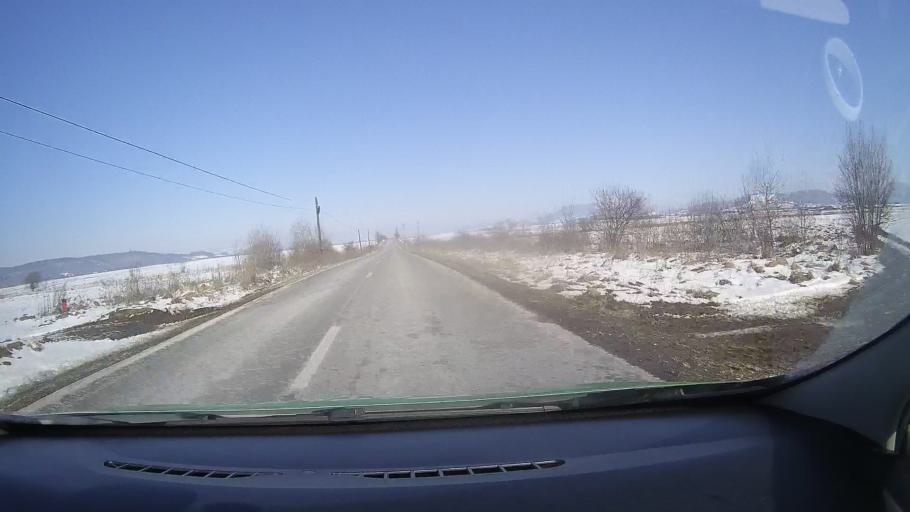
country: RO
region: Brasov
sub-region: Comuna Parau
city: Parau
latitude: 45.8544
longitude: 25.1949
